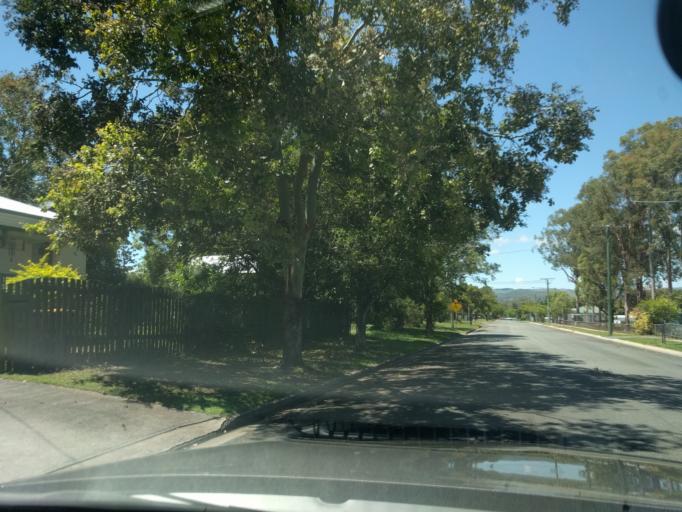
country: AU
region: Queensland
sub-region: Logan
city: Cedar Vale
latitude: -27.9883
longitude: 153.0047
